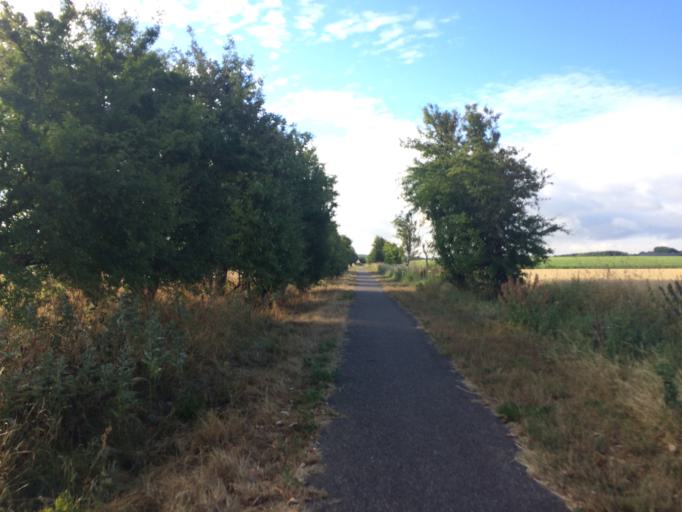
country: DK
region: Central Jutland
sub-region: Skive Kommune
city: Skive
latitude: 56.5968
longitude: 9.0006
